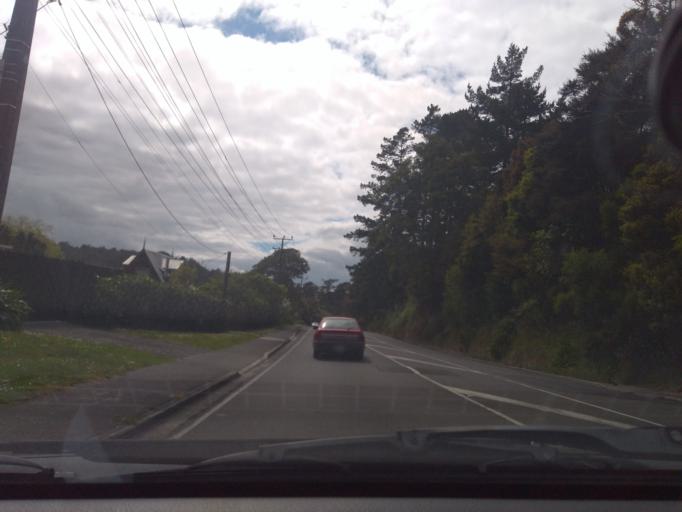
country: NZ
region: Auckland
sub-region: Auckland
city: Rosebank
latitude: -36.8650
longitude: 174.5672
